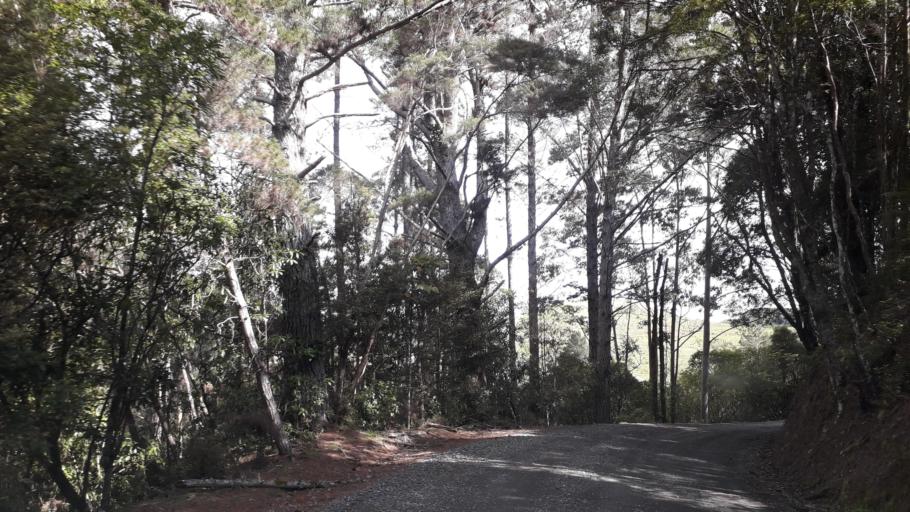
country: NZ
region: Northland
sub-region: Far North District
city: Taipa
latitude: -35.0995
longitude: 173.5506
